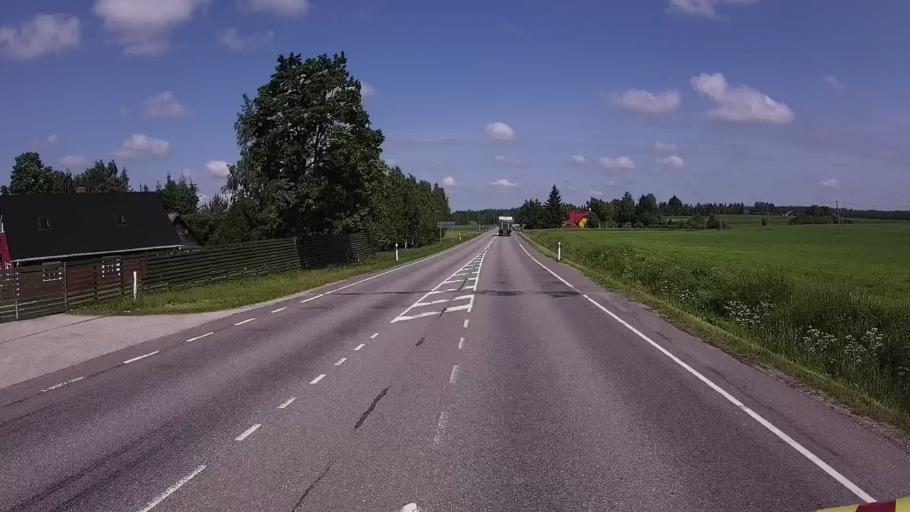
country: EE
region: Tartu
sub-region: UElenurme vald
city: Ulenurme
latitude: 58.2400
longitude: 26.7859
